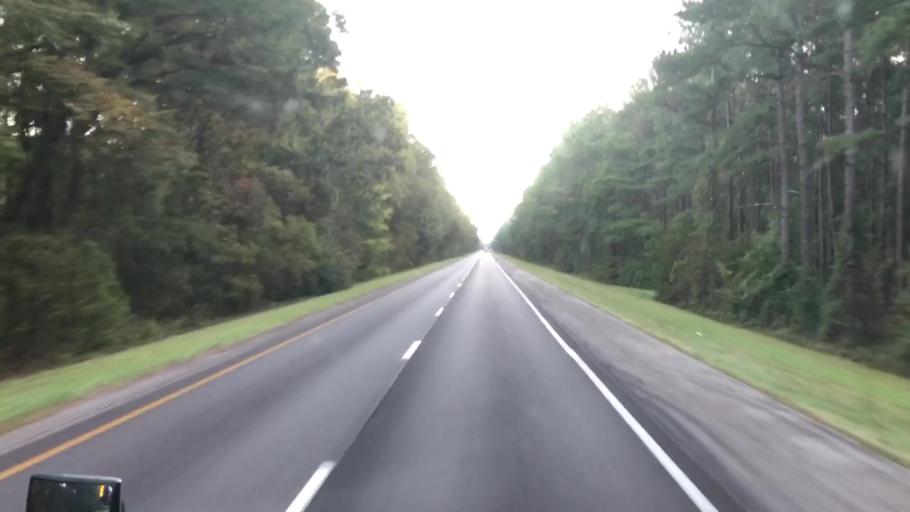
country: US
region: South Carolina
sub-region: Orangeburg County
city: Holly Hill
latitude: 33.5385
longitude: -80.4167
